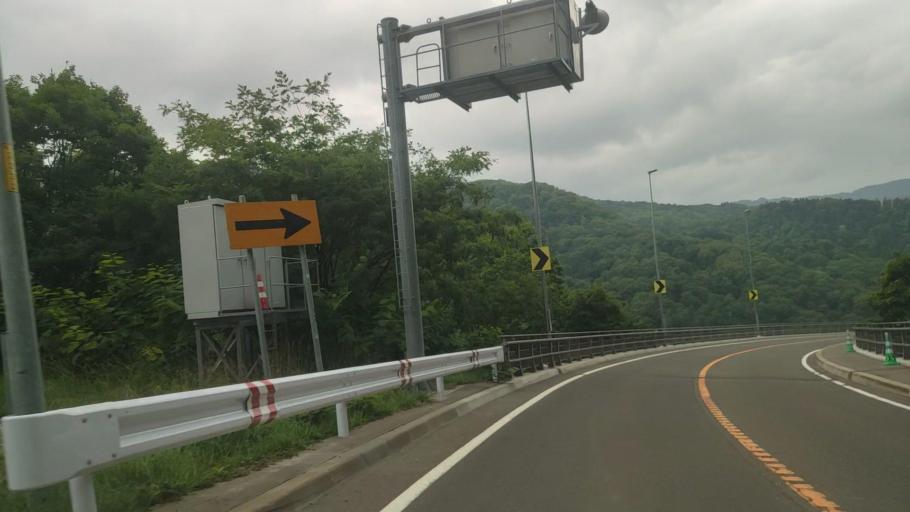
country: JP
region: Hokkaido
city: Sapporo
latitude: 42.9768
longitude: 141.1441
